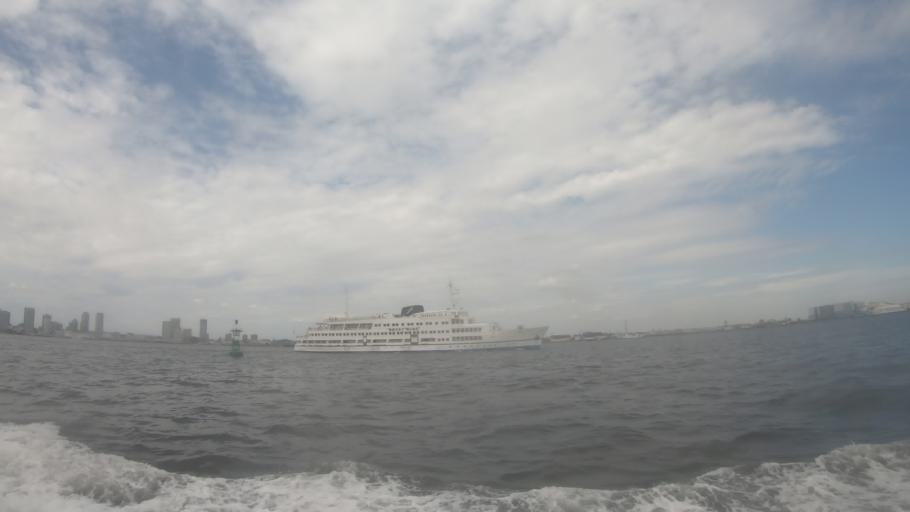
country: JP
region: Kanagawa
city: Yokohama
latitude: 35.4560
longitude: 139.6592
